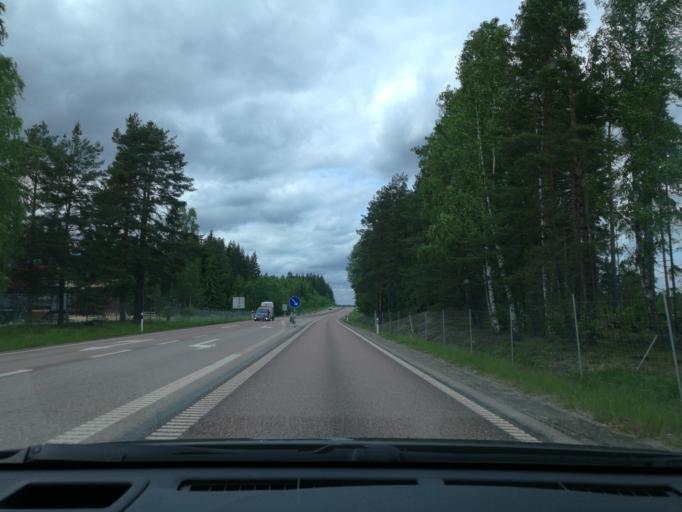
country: SE
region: Vaestmanland
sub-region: Fagersta Kommun
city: Fagersta
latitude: 59.9652
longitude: 15.8381
